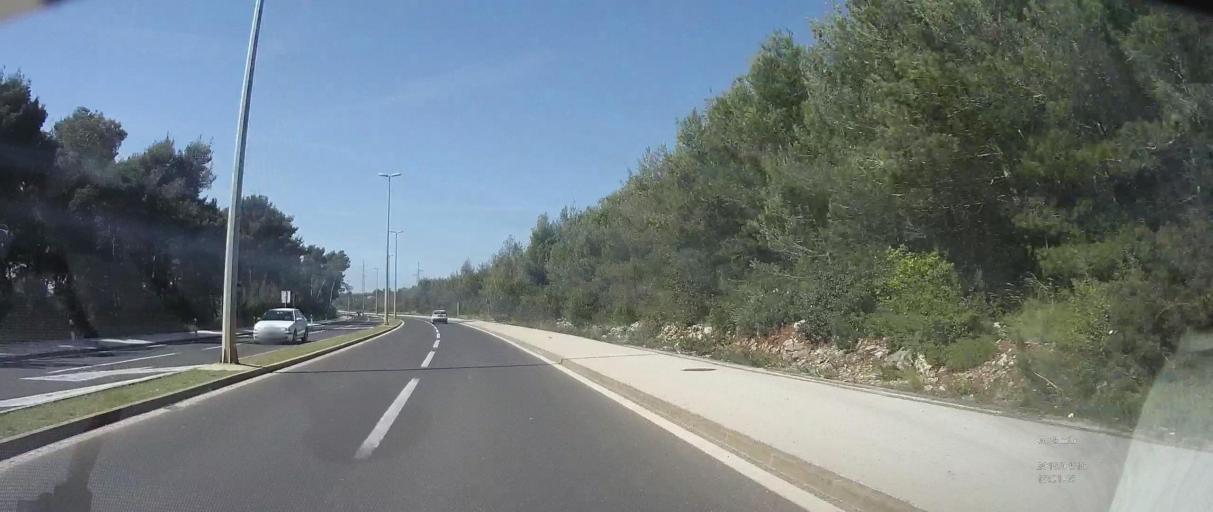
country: HR
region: Zadarska
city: Bibinje
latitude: 44.0856
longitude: 15.2836
